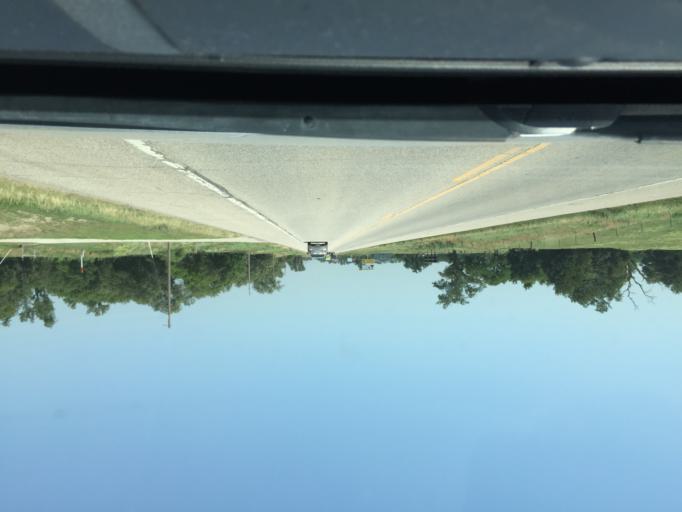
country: US
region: Kansas
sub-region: Reno County
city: South Hutchinson
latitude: 37.9866
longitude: -97.8668
